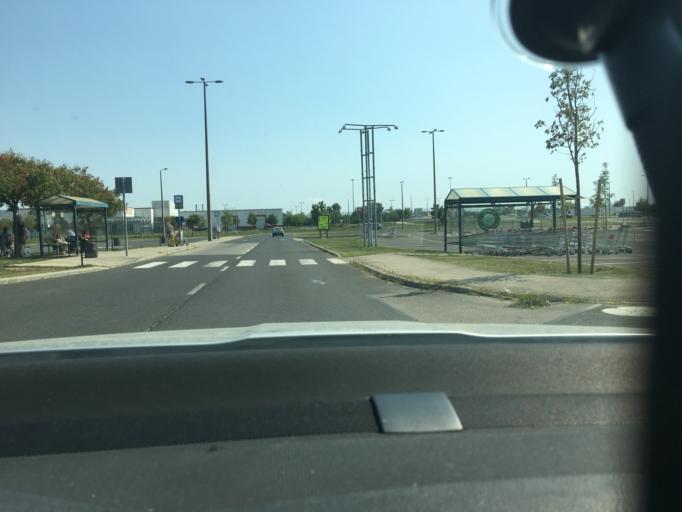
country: HU
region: Pest
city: Csomor
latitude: 47.5416
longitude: 19.2463
